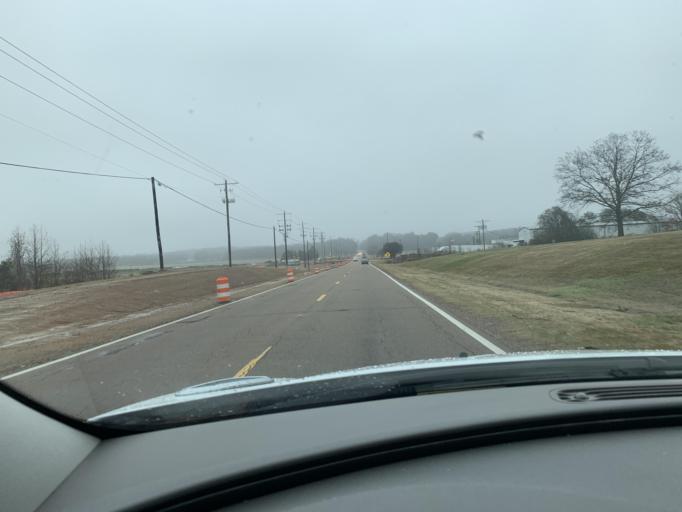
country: US
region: Mississippi
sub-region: De Soto County
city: Hernando
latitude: 34.8646
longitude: -89.9953
